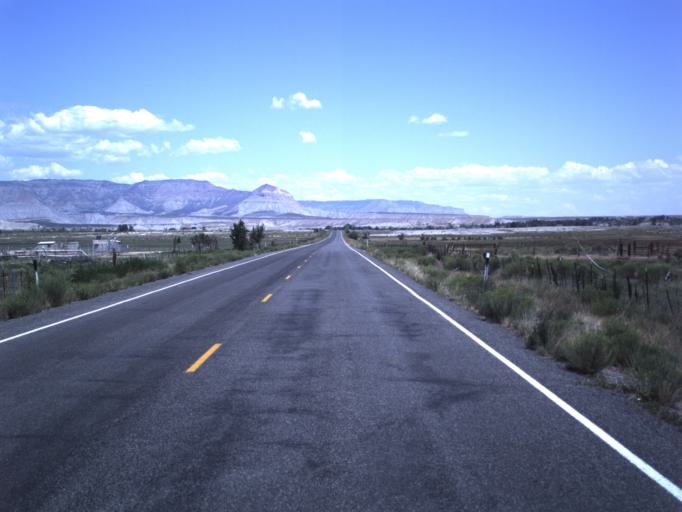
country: US
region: Utah
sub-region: Emery County
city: Castle Dale
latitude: 39.1927
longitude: -111.0477
